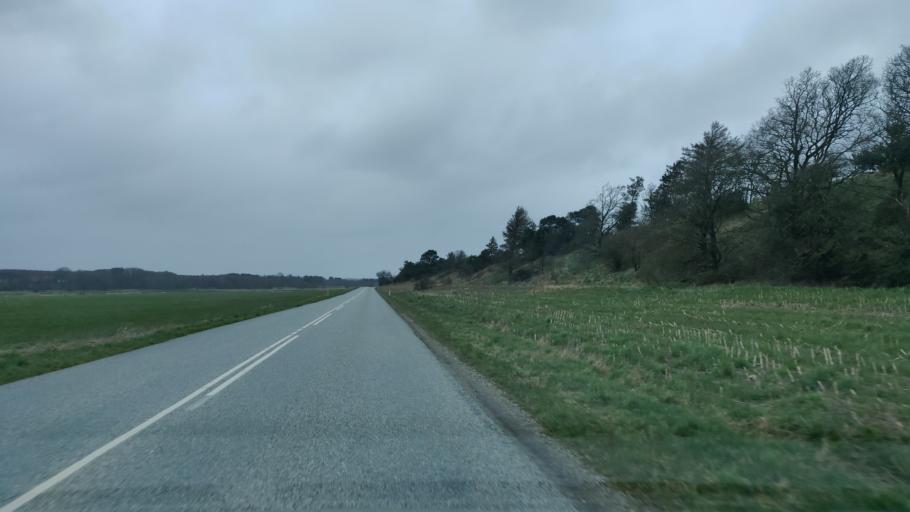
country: DK
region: Central Jutland
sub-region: Skive Kommune
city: Hojslev
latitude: 56.5653
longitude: 9.2496
